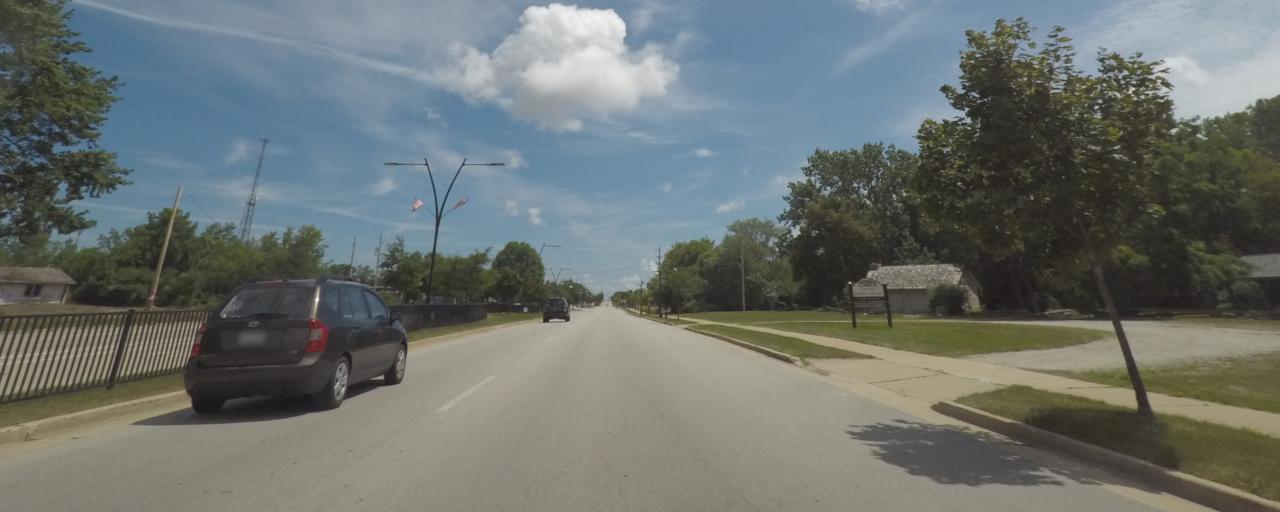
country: US
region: Wisconsin
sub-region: Milwaukee County
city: Greendale
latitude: 42.9593
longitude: -87.9850
